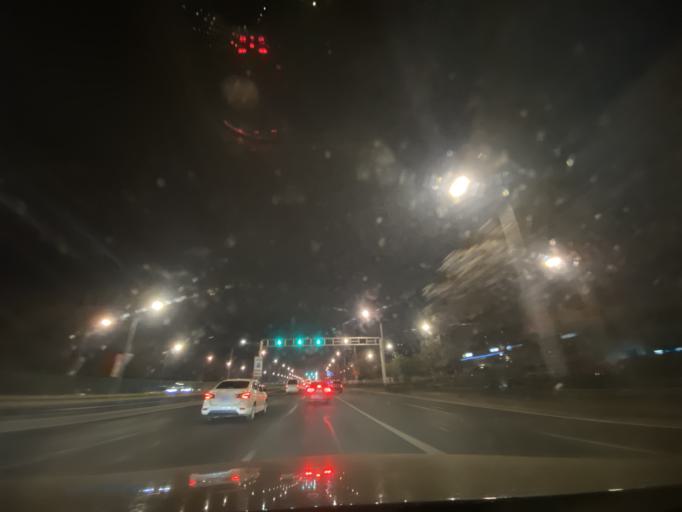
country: CN
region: Beijing
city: Babaoshan
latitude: 39.8958
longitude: 116.2427
